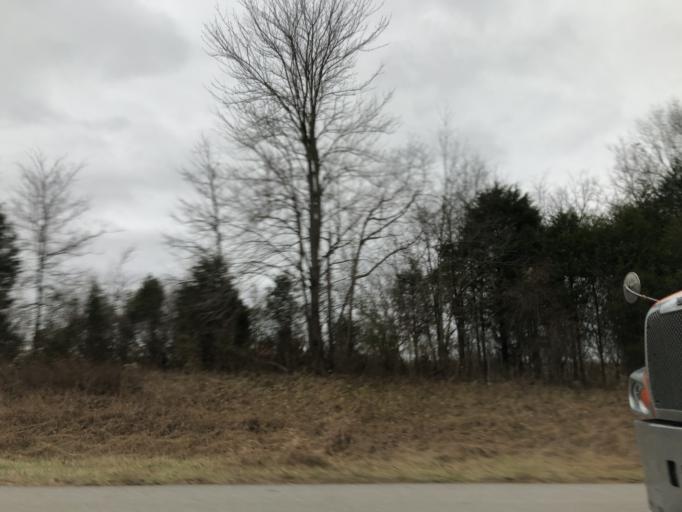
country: US
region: Illinois
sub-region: Johnson County
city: Vienna
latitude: 37.3733
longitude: -88.8121
